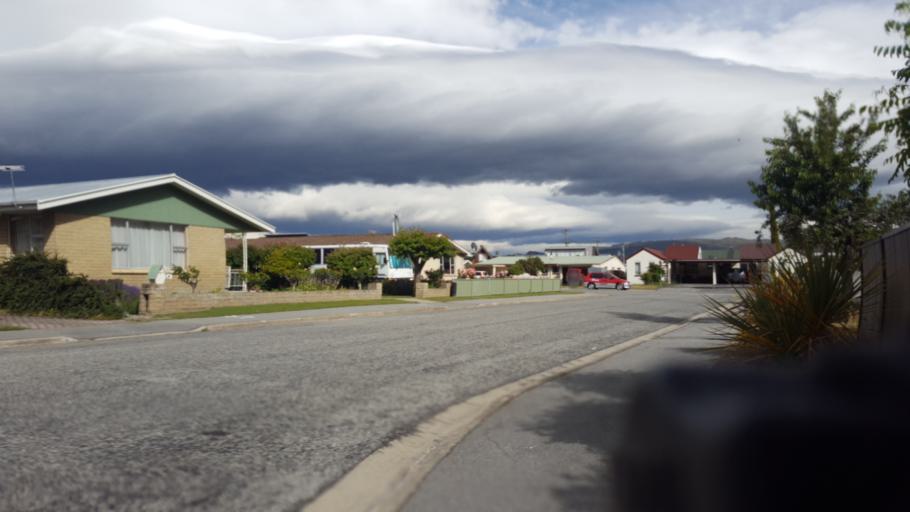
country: NZ
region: Otago
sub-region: Queenstown-Lakes District
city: Wanaka
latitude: -45.2495
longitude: 169.4007
